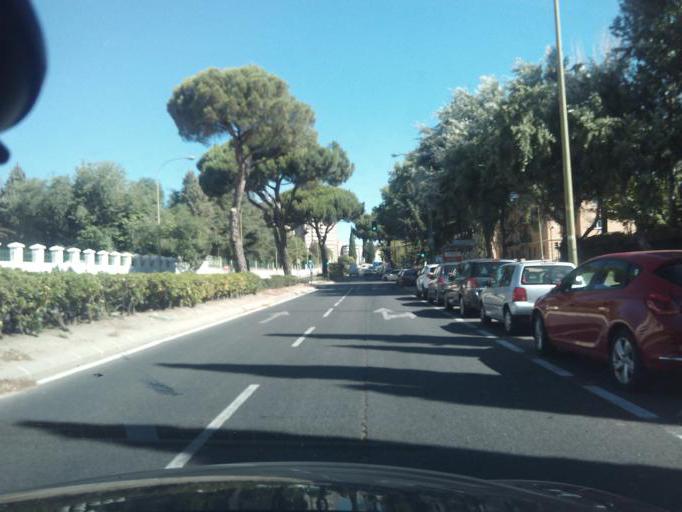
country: ES
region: Madrid
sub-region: Provincia de Madrid
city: Pinar de Chamartin
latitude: 40.4727
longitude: -3.6676
